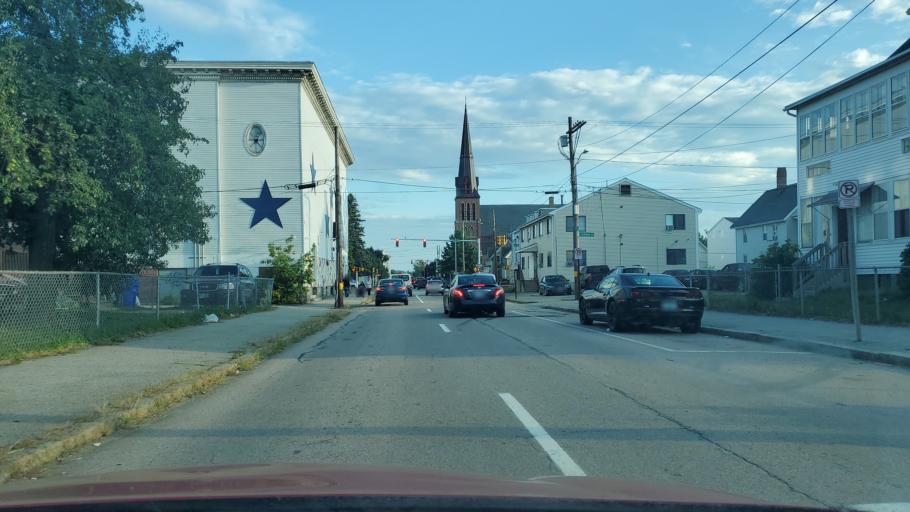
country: US
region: New Hampshire
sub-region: Hillsborough County
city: Manchester
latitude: 42.9880
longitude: -71.4553
